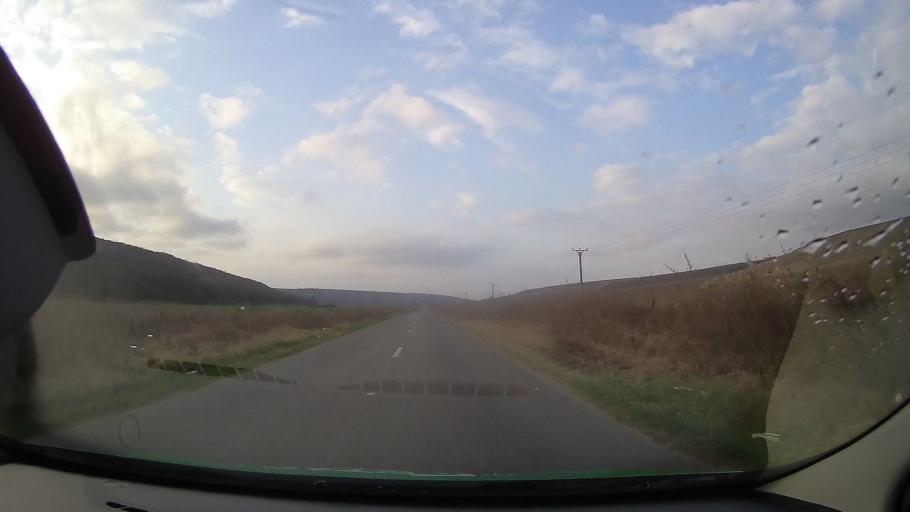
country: RO
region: Constanta
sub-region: Comuna Dobromir
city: Dobromir
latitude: 44.0299
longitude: 27.8604
